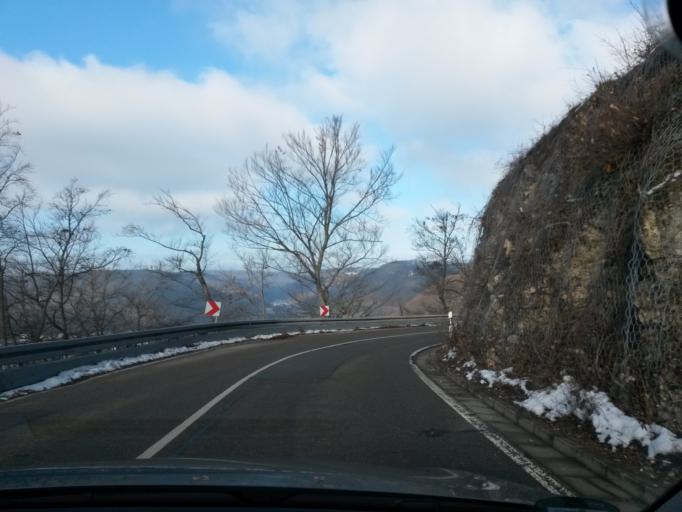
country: DE
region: Baden-Wuerttemberg
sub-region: Regierungsbezirk Stuttgart
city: Geislingen an der Steige
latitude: 48.6177
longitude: 9.8495
